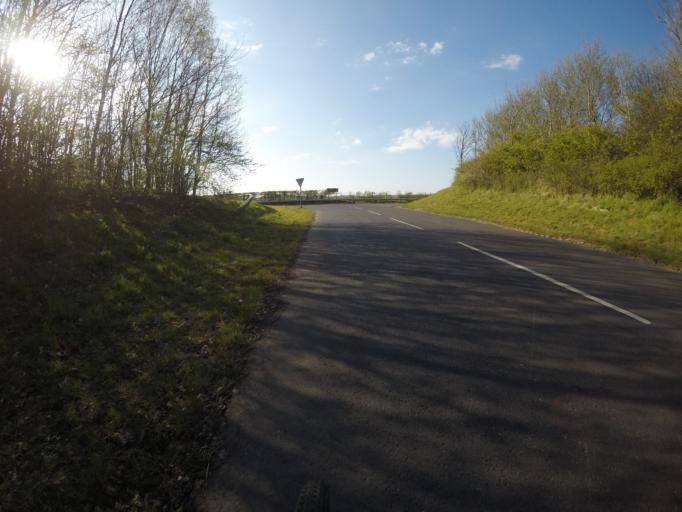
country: GB
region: Scotland
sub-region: North Ayrshire
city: Stevenston
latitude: 55.6515
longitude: -4.7409
